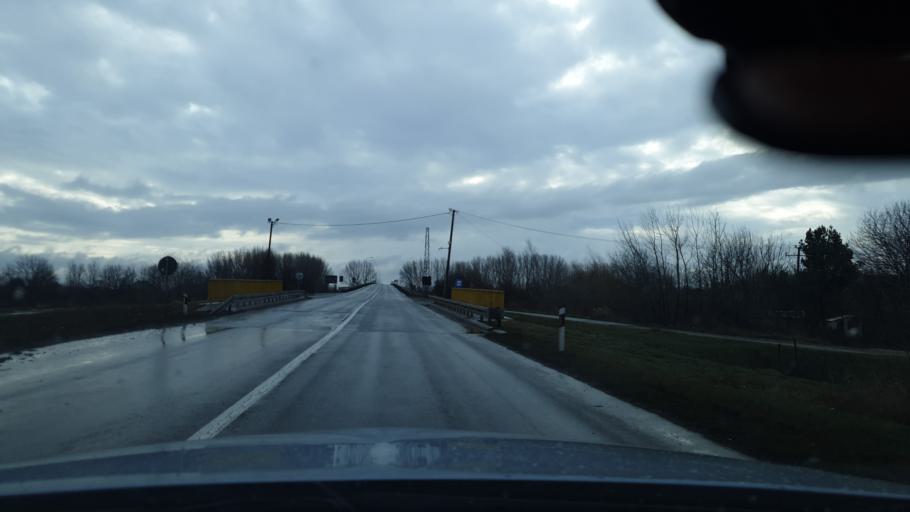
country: RS
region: Central Serbia
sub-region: Podunavski Okrug
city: Smederevo
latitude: 44.7046
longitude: 20.9442
